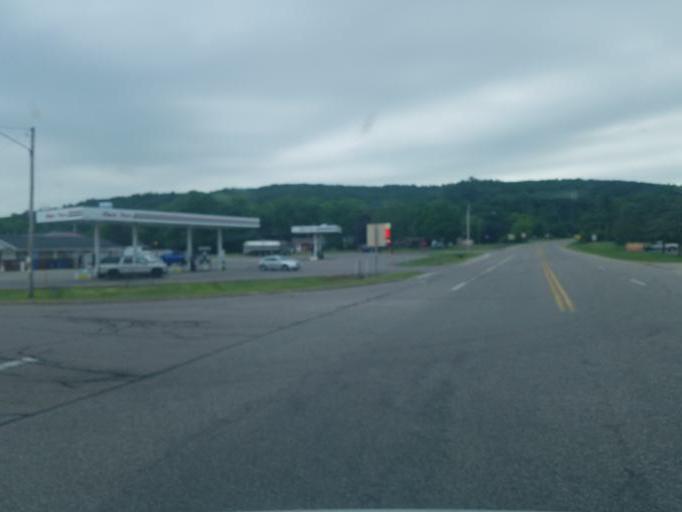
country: US
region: Wisconsin
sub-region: Juneau County
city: Elroy
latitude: 43.6810
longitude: -90.2662
